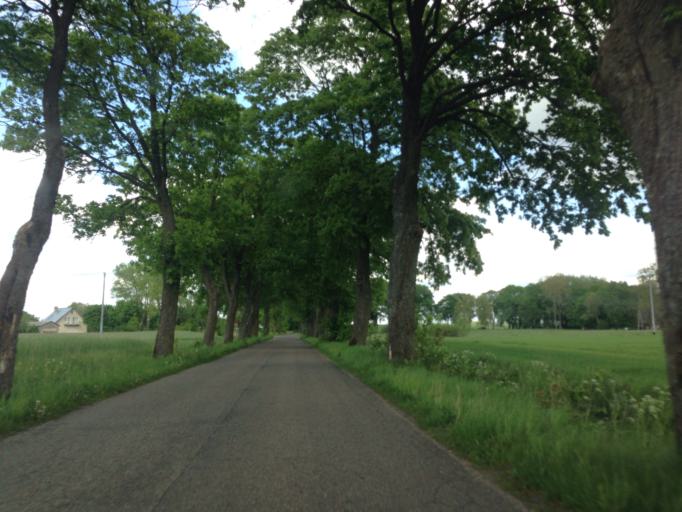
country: PL
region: Warmian-Masurian Voivodeship
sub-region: Powiat ostrodzki
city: Dabrowno
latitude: 53.3906
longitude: 20.1321
